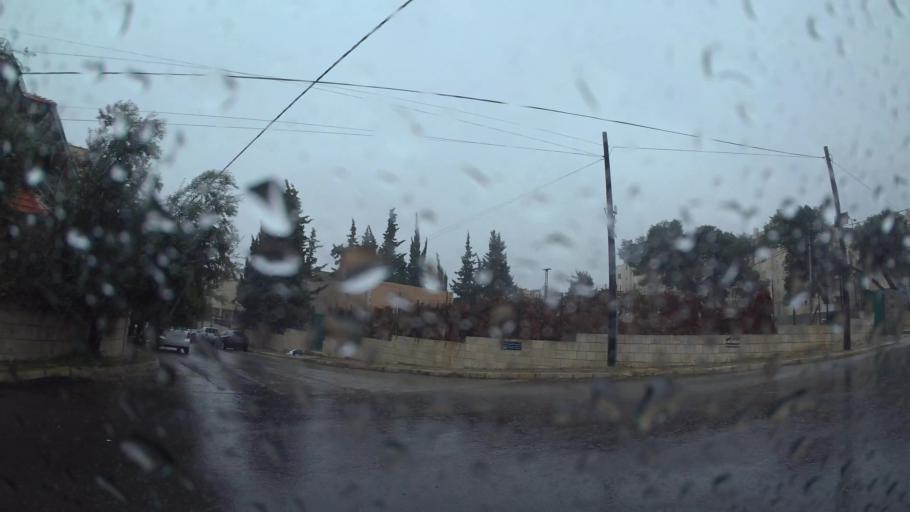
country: JO
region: Amman
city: Al Jubayhah
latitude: 32.0302
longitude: 35.8885
